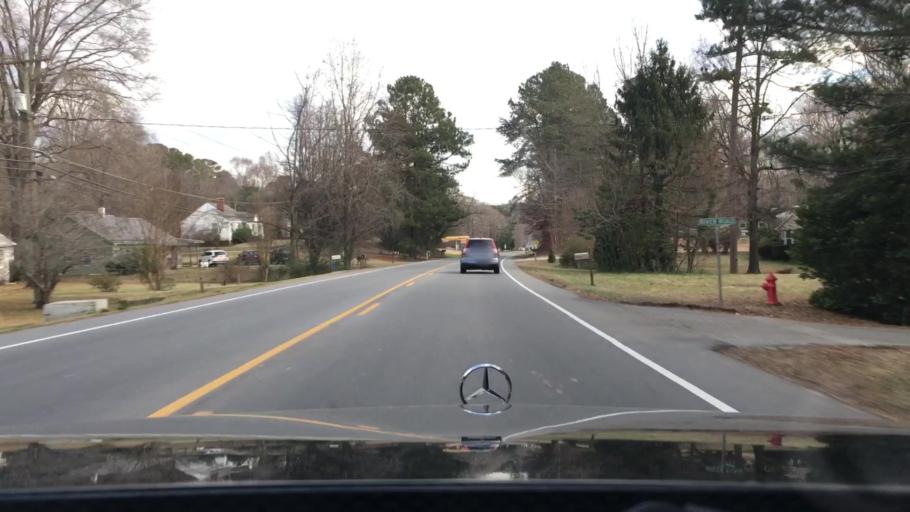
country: US
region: North Carolina
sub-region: Orange County
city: Hillsborough
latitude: 36.0810
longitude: -79.0779
